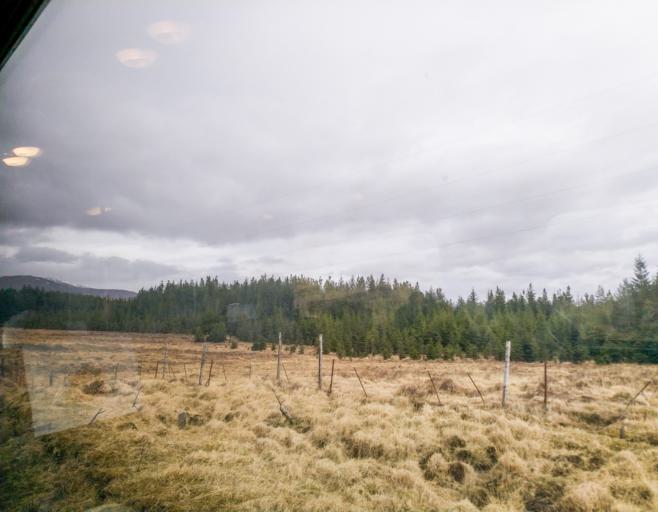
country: GB
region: Scotland
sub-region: Highland
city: Spean Bridge
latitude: 56.6617
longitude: -4.5643
